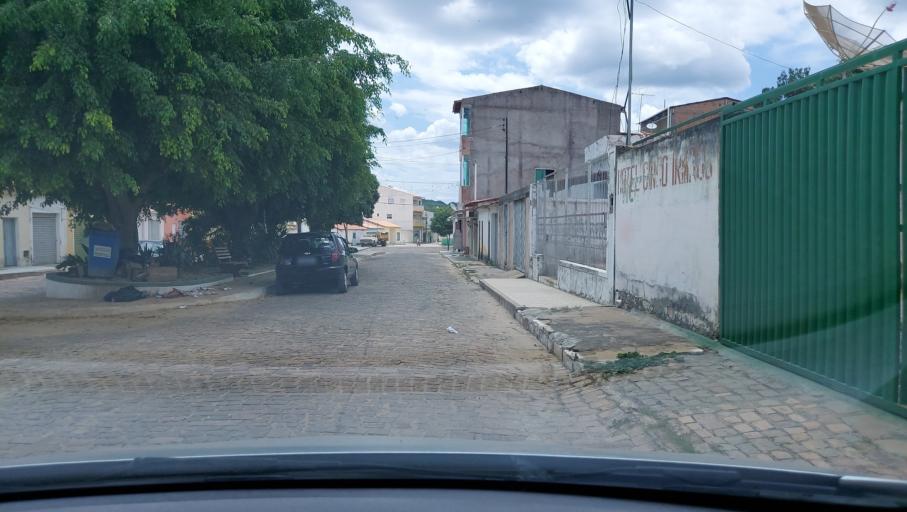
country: BR
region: Bahia
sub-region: Oliveira Dos Brejinhos
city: Beira Rio
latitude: -12.0010
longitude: -42.6267
